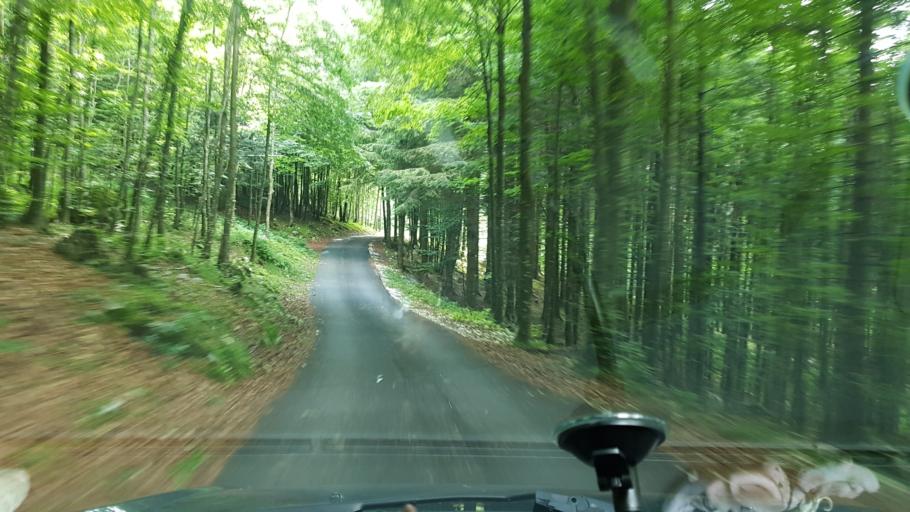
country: IT
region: Friuli Venezia Giulia
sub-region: Provincia di Udine
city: Taipana
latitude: 46.3317
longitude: 13.4211
